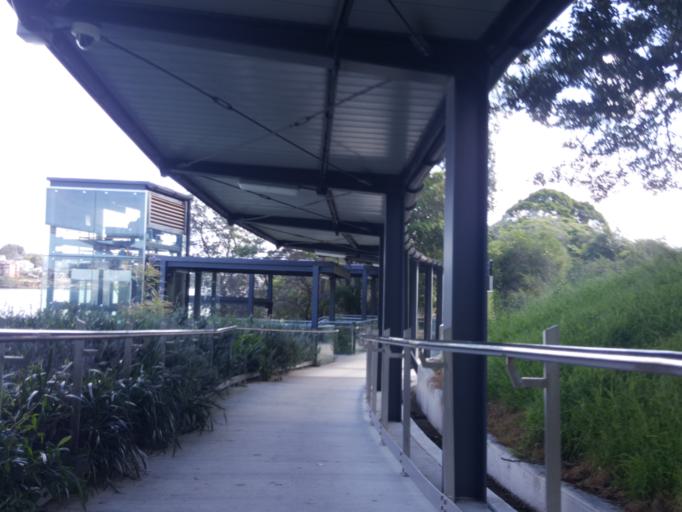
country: AU
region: New South Wales
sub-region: Canada Bay
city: Canada Bay
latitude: -33.8470
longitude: 151.1406
